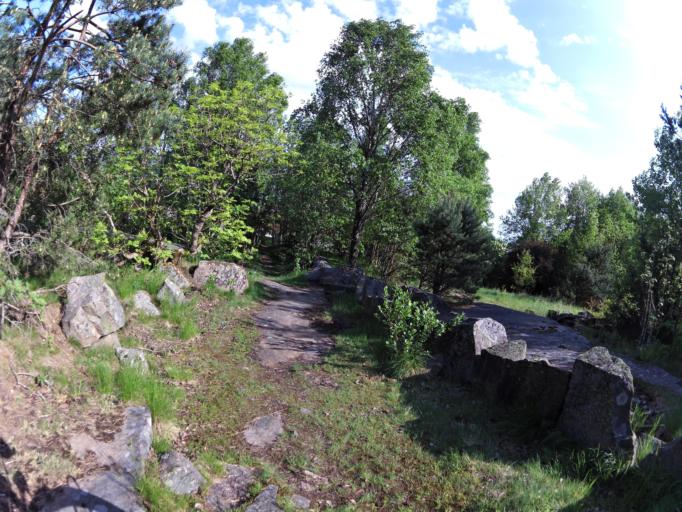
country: NO
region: Ostfold
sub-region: Fredrikstad
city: Fredrikstad
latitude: 59.2367
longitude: 10.9729
